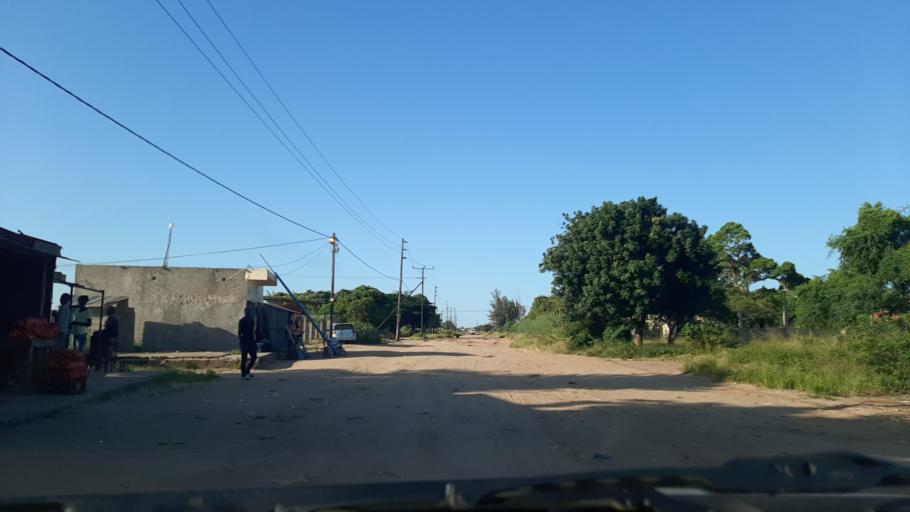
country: MZ
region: Maputo City
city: Maputo
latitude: -25.7625
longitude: 32.5477
